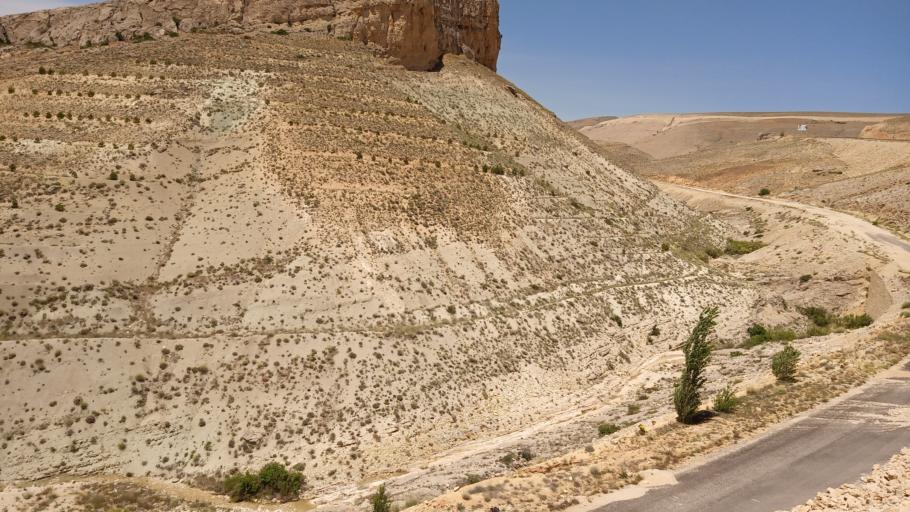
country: TR
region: Malatya
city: Darende
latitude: 38.5768
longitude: 37.4648
